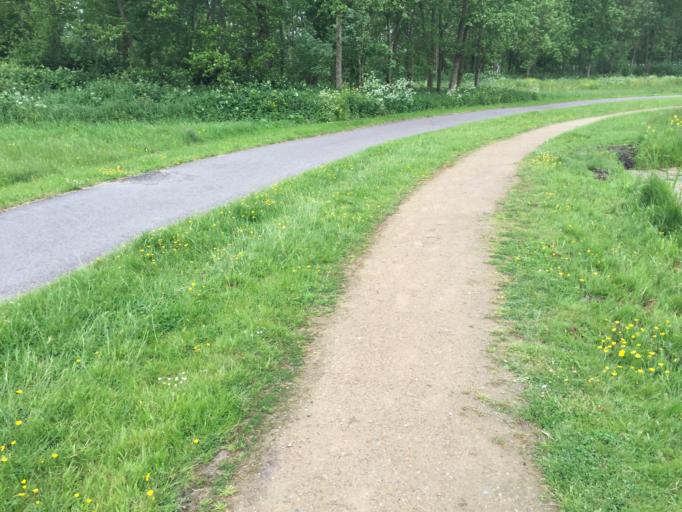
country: NL
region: South Holland
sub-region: Bodegraven-Reeuwijk
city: Reeuwijk
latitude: 52.0172
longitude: 4.7441
